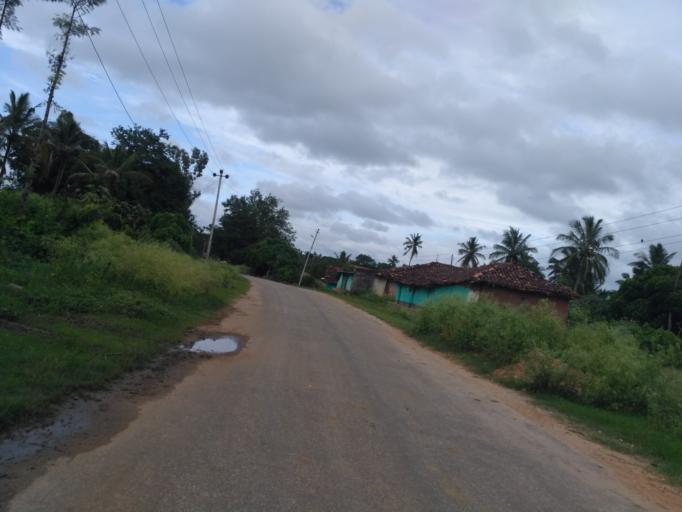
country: IN
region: Karnataka
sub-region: Hassan
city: Gorur
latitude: 12.8234
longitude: 76.0875
